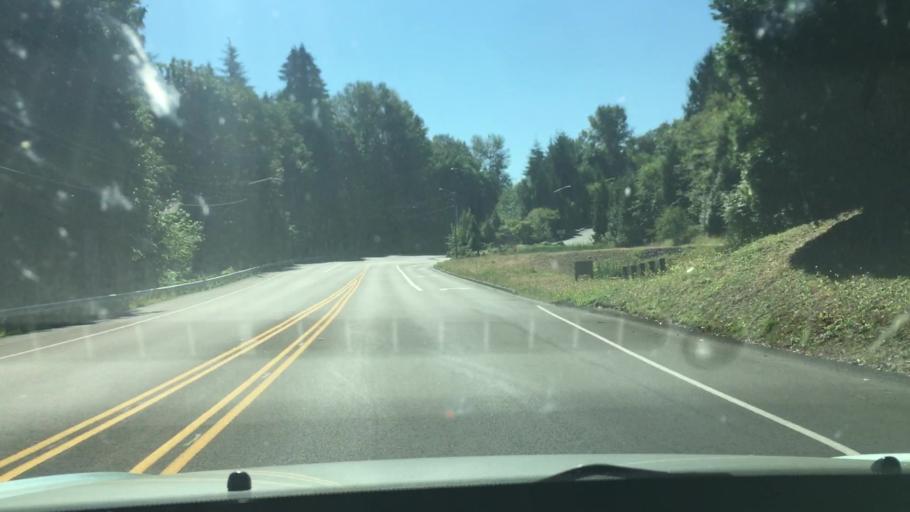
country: US
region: Washington
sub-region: King County
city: Newcastle
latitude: 47.5374
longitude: -122.1346
